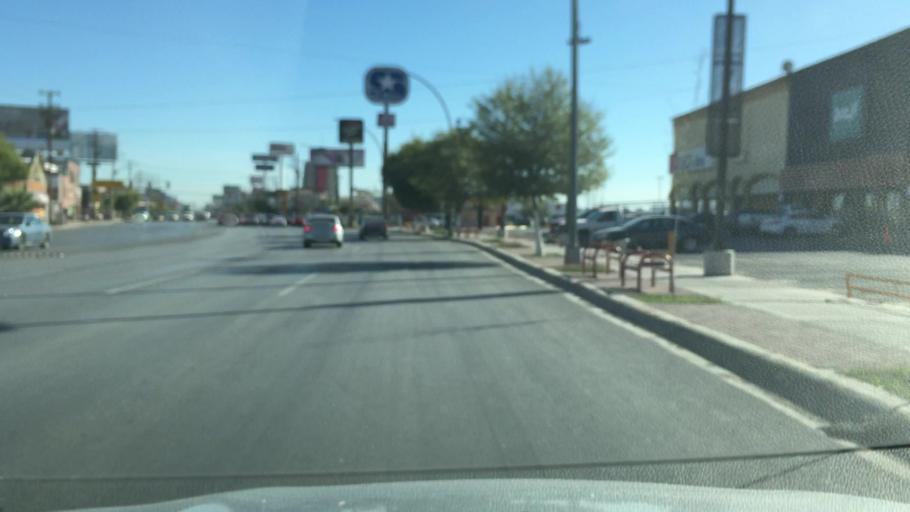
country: MX
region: Chihuahua
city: Ciudad Juarez
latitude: 31.7368
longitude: -106.4471
